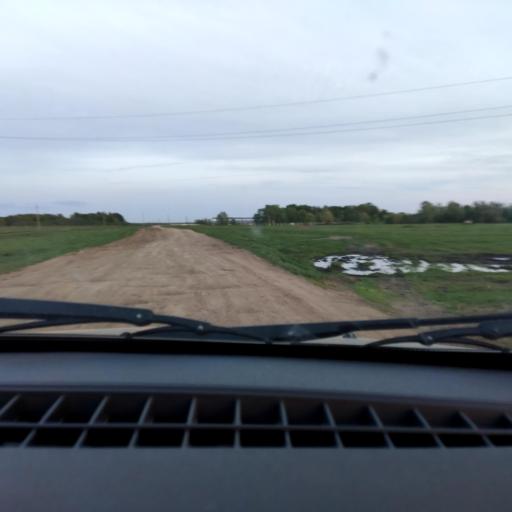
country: RU
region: Bashkortostan
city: Iglino
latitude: 54.9115
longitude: 56.3927
